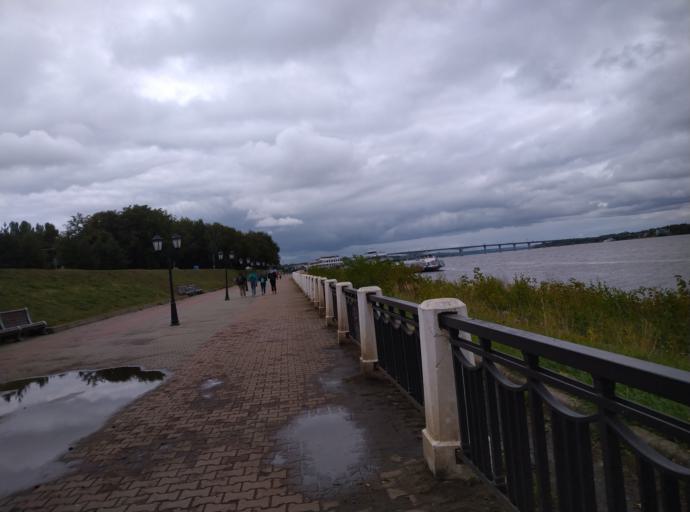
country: RU
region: Kostroma
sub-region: Kostromskoy Rayon
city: Kostroma
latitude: 57.7633
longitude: 40.9237
